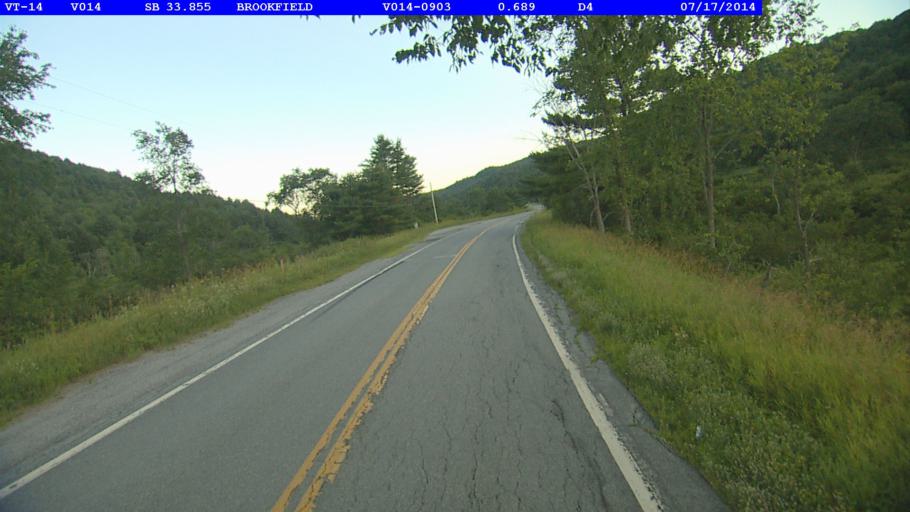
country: US
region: Vermont
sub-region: Orange County
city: Chelsea
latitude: 43.9889
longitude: -72.5562
